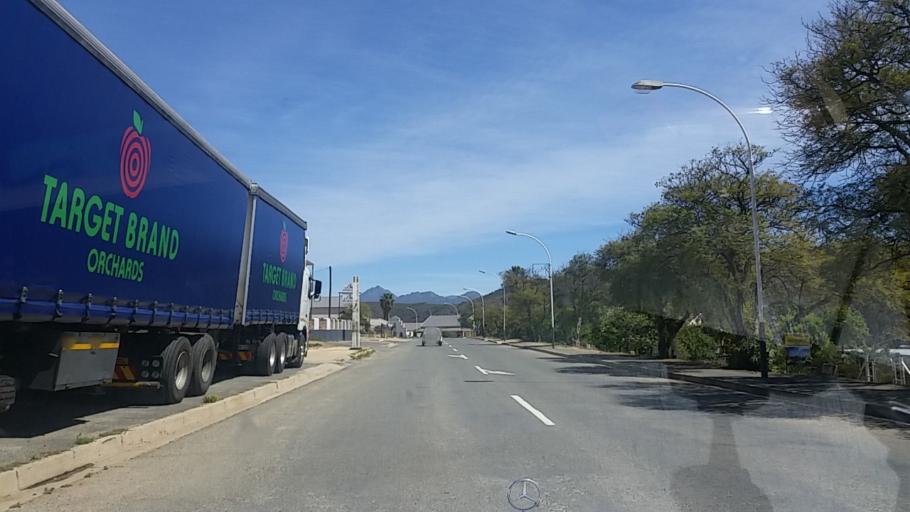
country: ZA
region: Western Cape
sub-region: Eden District Municipality
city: Knysna
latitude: -33.6551
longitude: 23.1322
